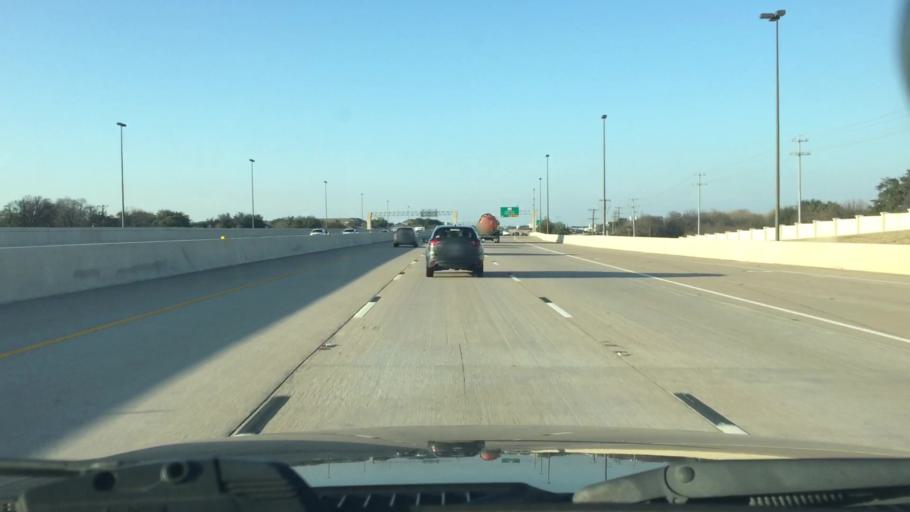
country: US
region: Texas
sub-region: Williamson County
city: Cedar Park
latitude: 30.5163
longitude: -97.8138
